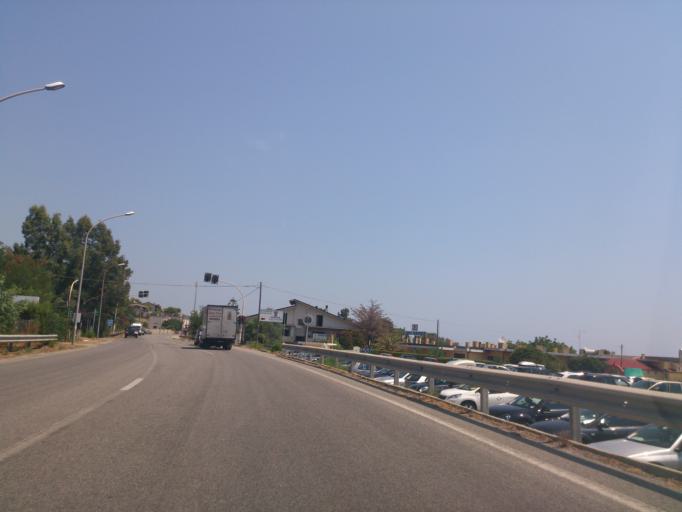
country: IT
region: Calabria
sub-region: Provincia di Reggio Calabria
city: Riace Marina
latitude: 38.3865
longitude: 16.5262
